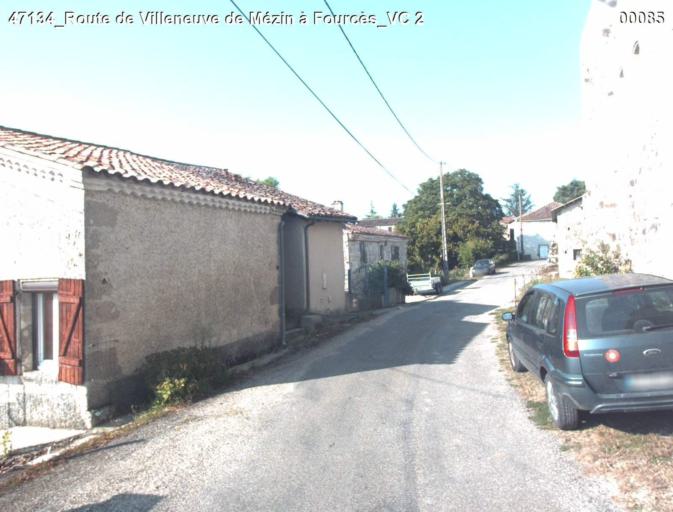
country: FR
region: Aquitaine
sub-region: Departement du Lot-et-Garonne
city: Mezin
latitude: 44.0162
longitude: 0.2469
